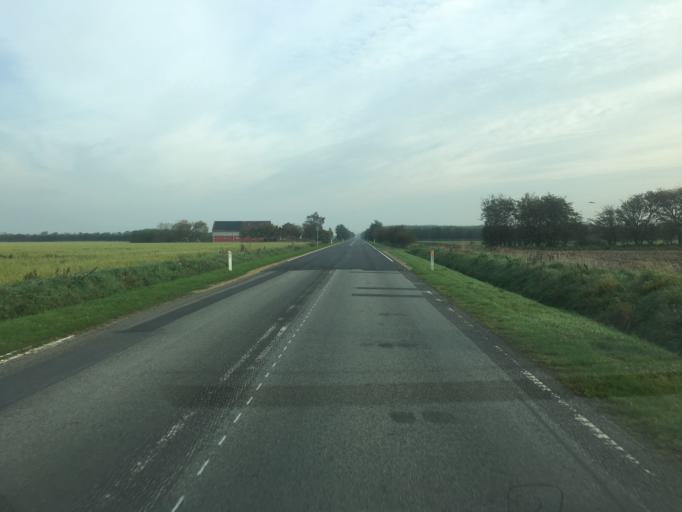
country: DK
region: South Denmark
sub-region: Tonder Kommune
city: Logumkloster
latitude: 55.0670
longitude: 8.9615
